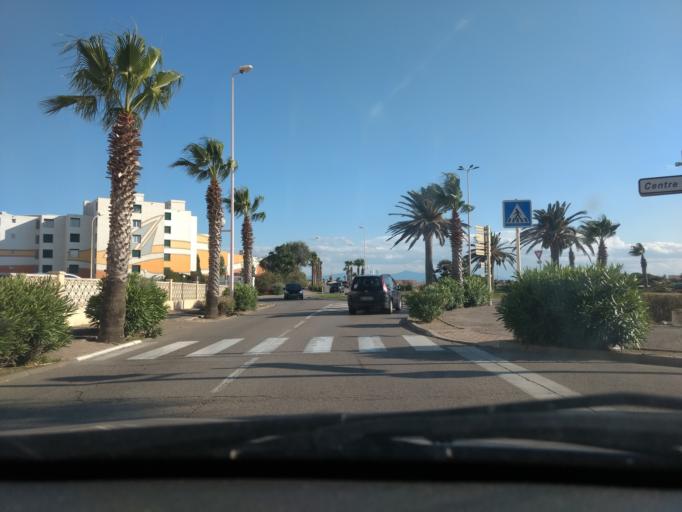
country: FR
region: Languedoc-Roussillon
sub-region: Departement des Pyrenees-Orientales
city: Le Barcares
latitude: 42.8005
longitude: 3.0370
